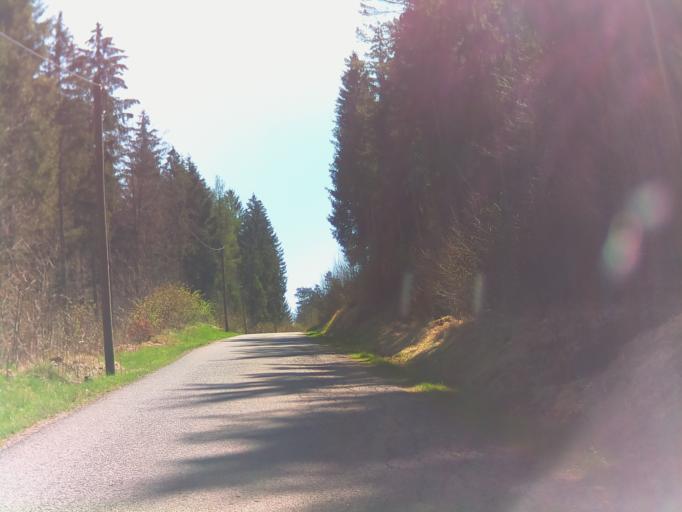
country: DE
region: Bavaria
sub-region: Upper Palatinate
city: Kastl
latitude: 49.3850
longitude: 11.6886
